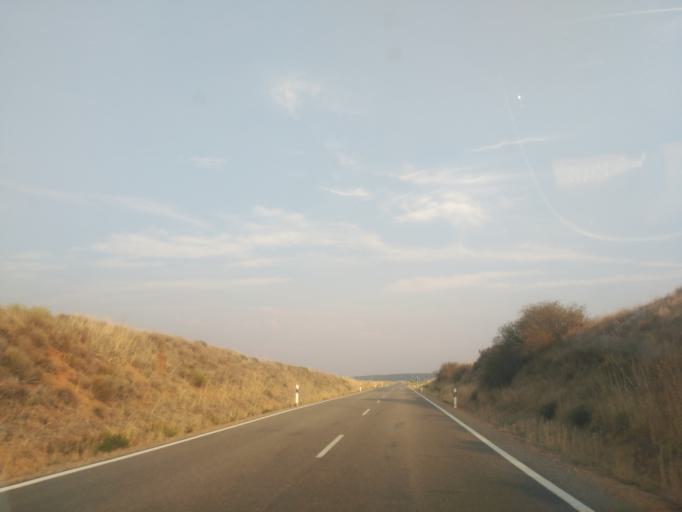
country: ES
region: Castille and Leon
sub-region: Provincia de Zamora
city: Pozuelo de Tabara
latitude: 41.7754
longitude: -5.8815
